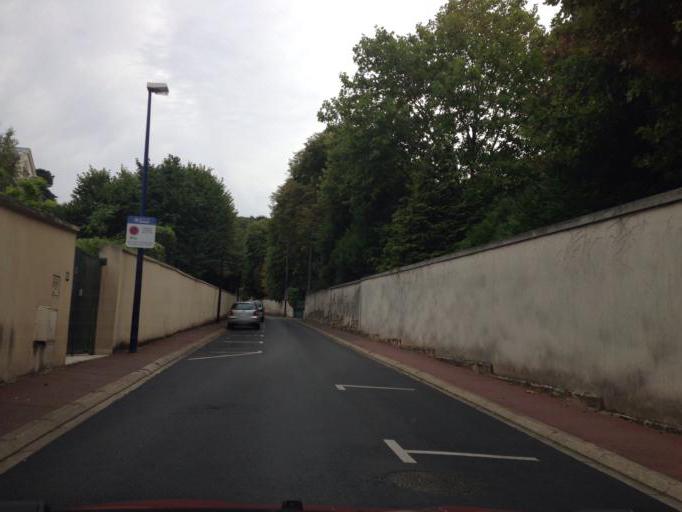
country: FR
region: Ile-de-France
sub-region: Departement des Hauts-de-Seine
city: Clamart
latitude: 48.7979
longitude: 2.2630
